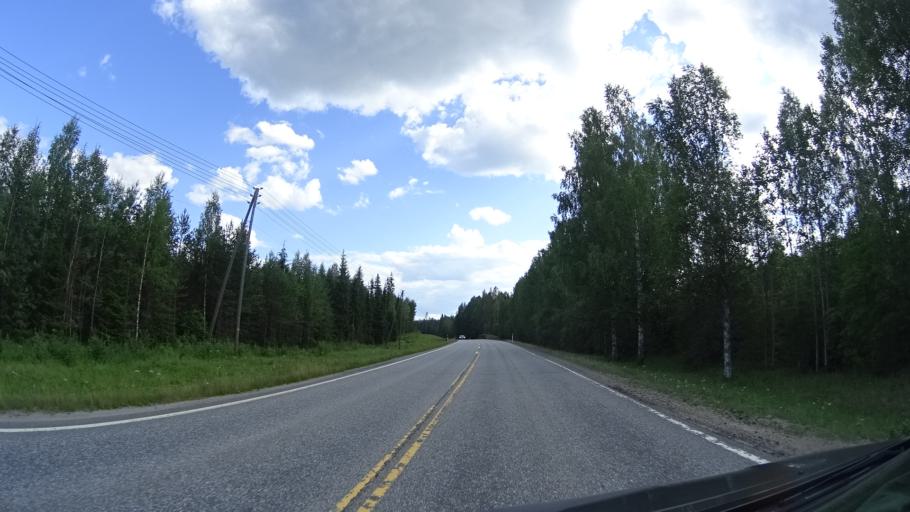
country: FI
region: Southern Savonia
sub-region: Savonlinna
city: Punkaharju
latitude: 61.6696
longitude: 29.4122
